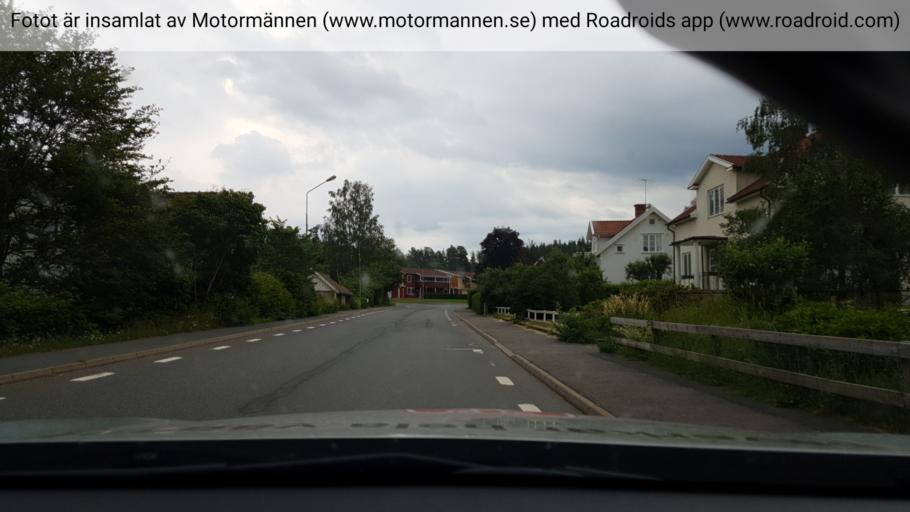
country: SE
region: Joenkoeping
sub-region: Mullsjo Kommun
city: Mullsjoe
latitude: 57.9850
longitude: 13.7762
